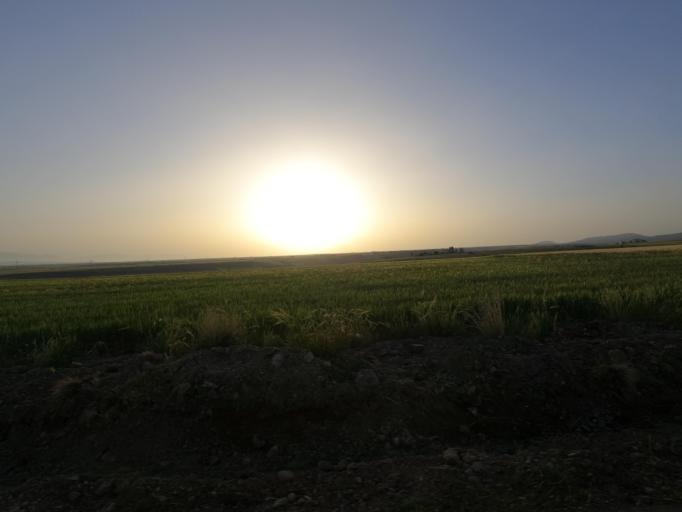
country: CY
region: Lefkosia
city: Astromeritis
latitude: 35.1116
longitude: 33.0144
